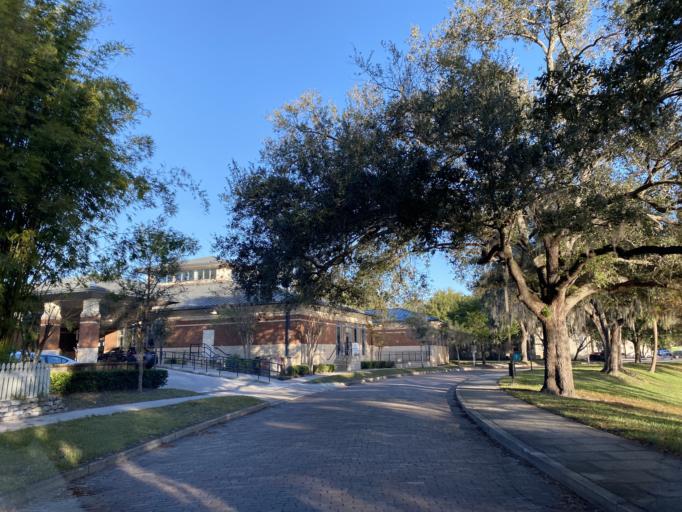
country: US
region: Florida
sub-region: Orange County
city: Orlando
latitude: 28.5517
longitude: -81.3876
